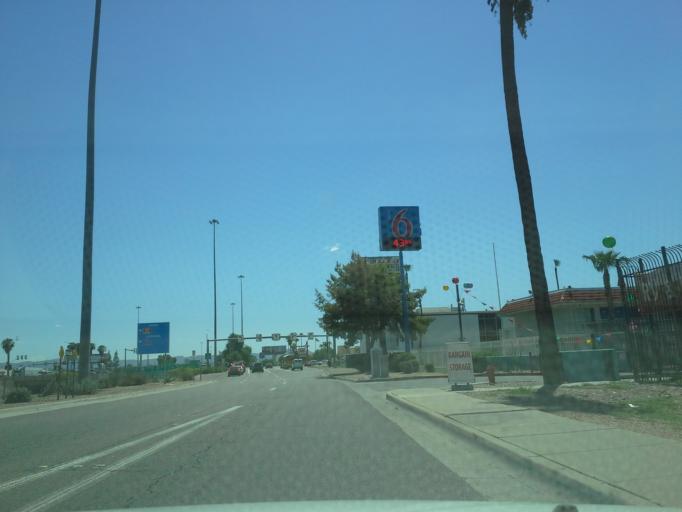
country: US
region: Arizona
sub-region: Maricopa County
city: Phoenix
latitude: 33.4969
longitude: -112.1134
